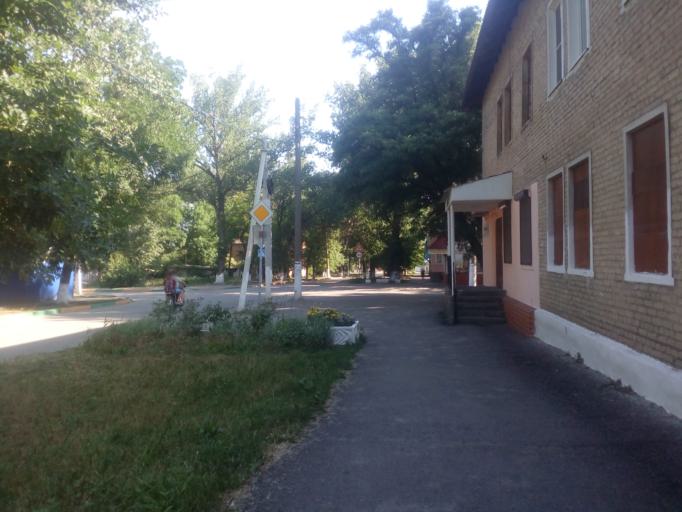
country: RU
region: Rostov
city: Sholokhovskiy
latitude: 48.2808
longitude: 41.0498
